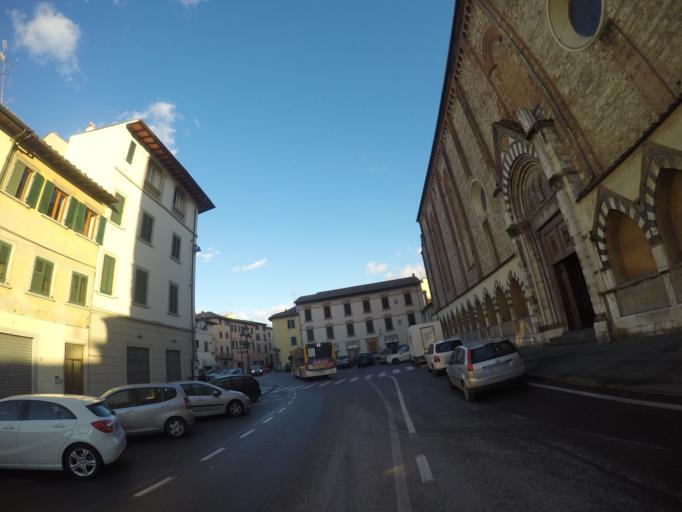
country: IT
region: Tuscany
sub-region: Provincia di Prato
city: Prato
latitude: 43.8818
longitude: 11.0939
